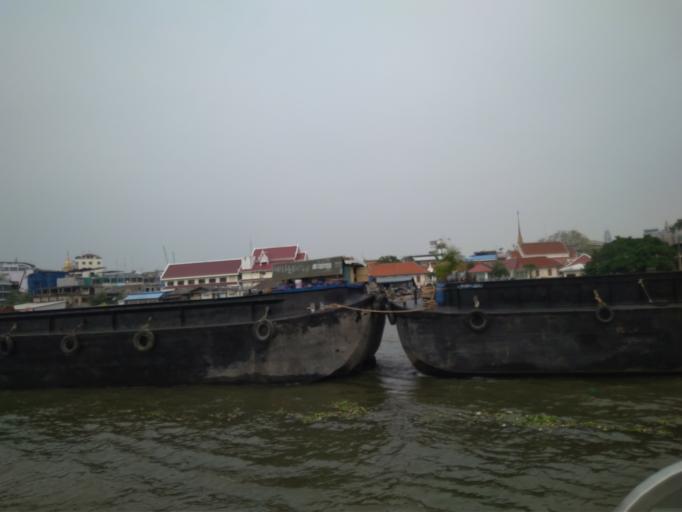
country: TH
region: Bangkok
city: Khlong San
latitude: 13.7344
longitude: 100.5096
